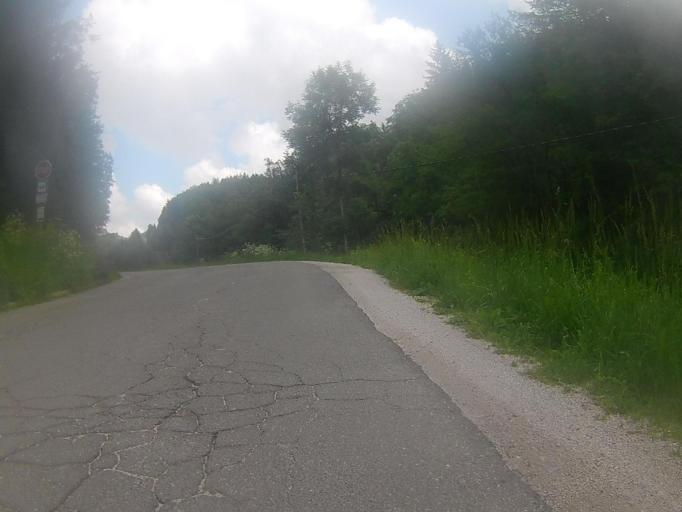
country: SI
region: Maribor
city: Bresternica
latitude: 46.6167
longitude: 15.5529
